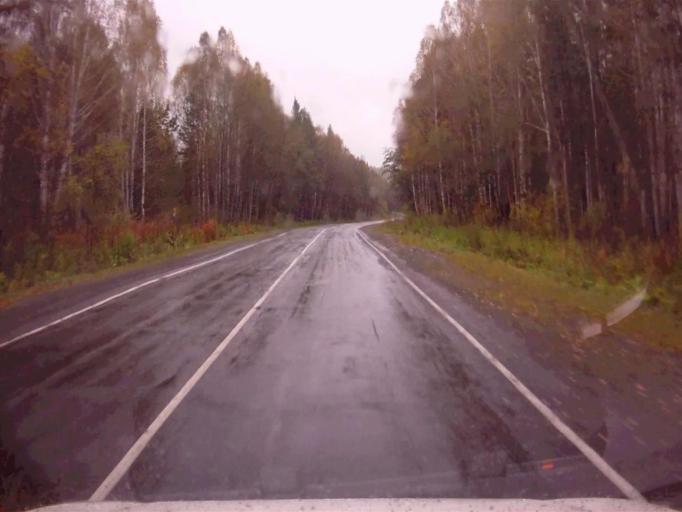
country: RU
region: Chelyabinsk
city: Verkhniy Ufaley
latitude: 55.9538
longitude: 60.3929
